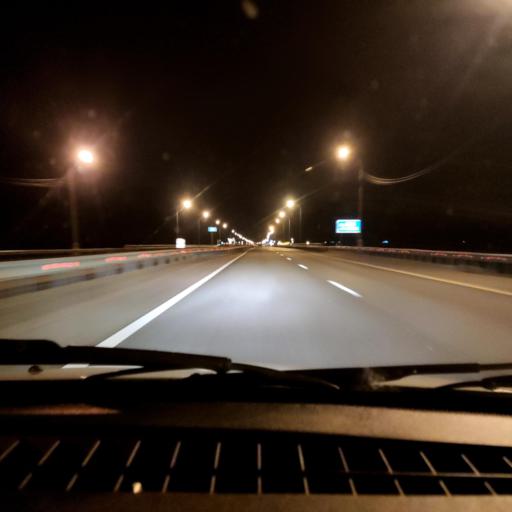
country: RU
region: Lipetsk
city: Zadonsk
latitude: 52.3727
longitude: 38.9059
